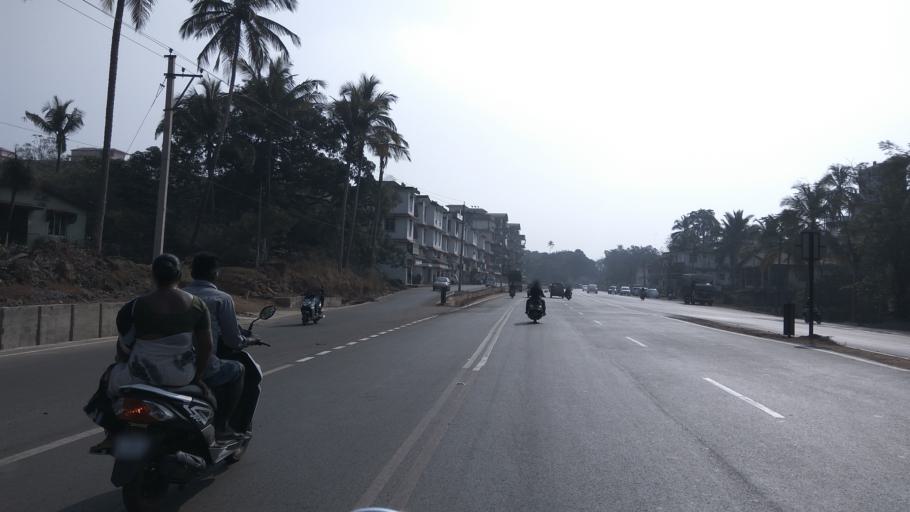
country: IN
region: Goa
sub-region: North Goa
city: Jua
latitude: 15.4988
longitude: 73.9197
